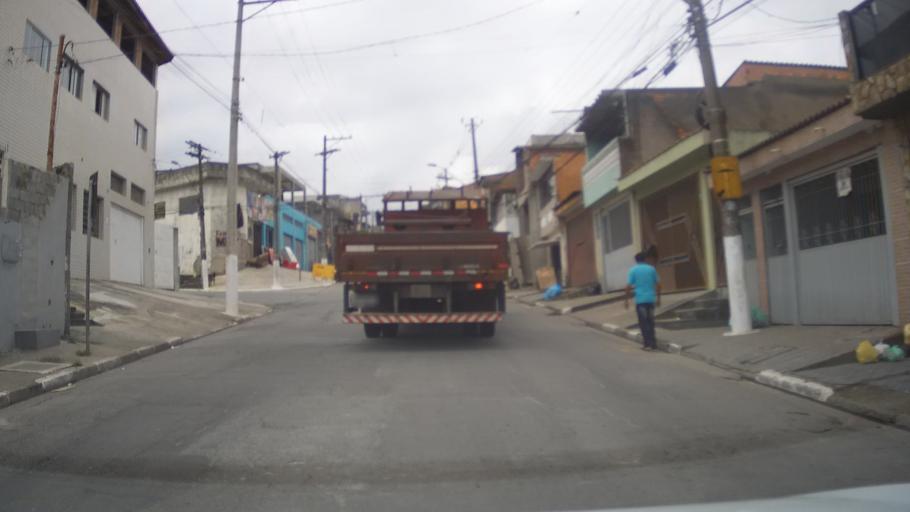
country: BR
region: Sao Paulo
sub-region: Itaquaquecetuba
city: Itaquaquecetuba
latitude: -23.4490
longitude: -46.4015
